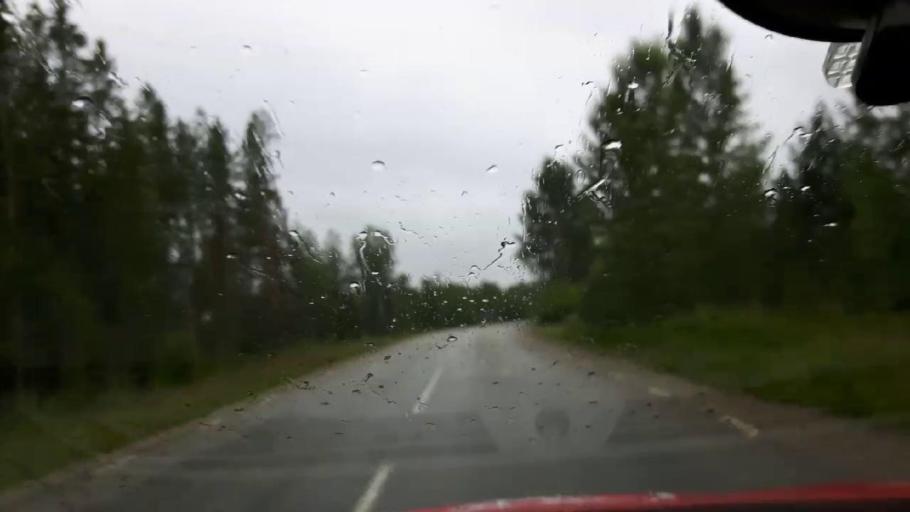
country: SE
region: Jaemtland
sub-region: OEstersunds Kommun
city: Brunflo
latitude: 62.8020
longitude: 15.0012
